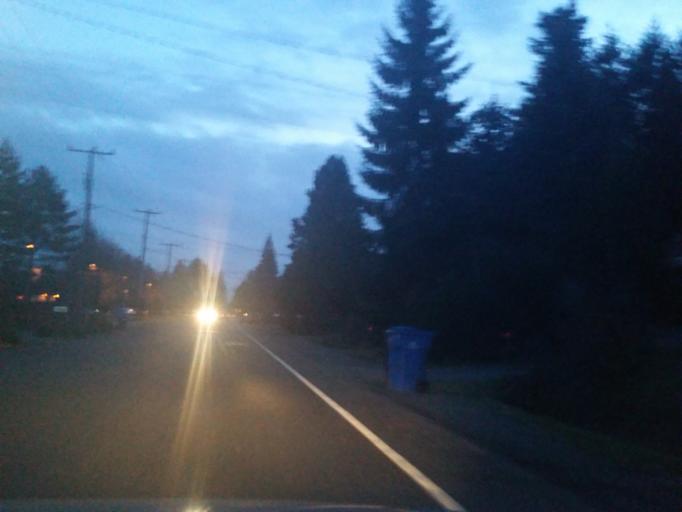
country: US
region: Washington
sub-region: King County
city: Shoreline
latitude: 47.7509
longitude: -122.3187
